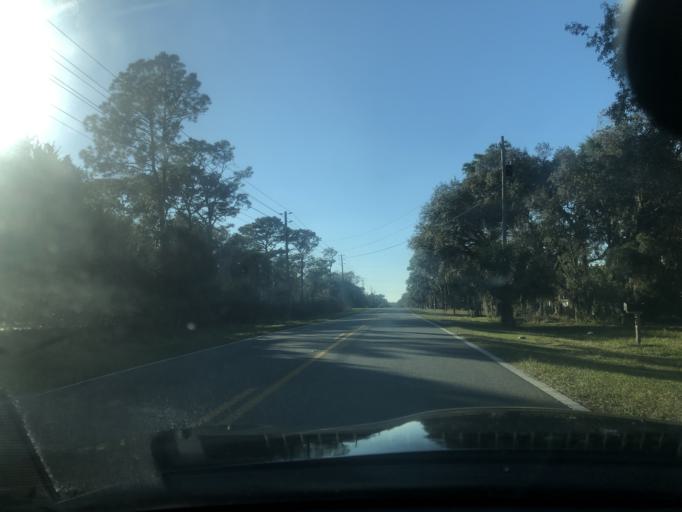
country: US
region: Florida
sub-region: Citrus County
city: Sugarmill Woods
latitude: 28.7641
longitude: -82.5345
